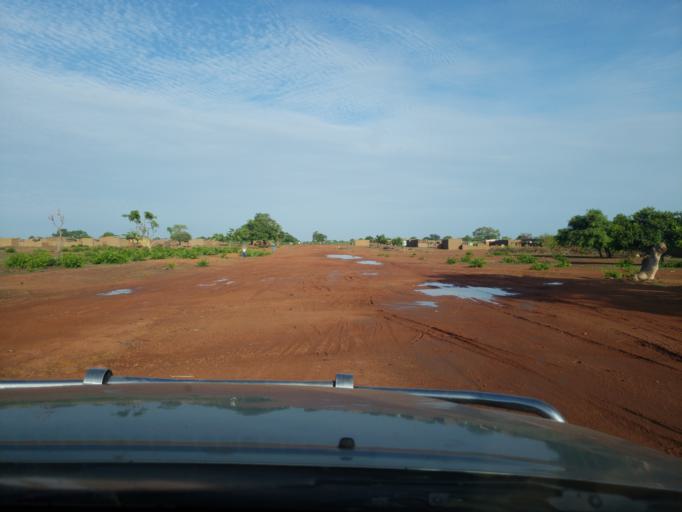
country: ML
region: Sikasso
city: Koutiala
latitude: 12.4288
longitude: -5.6201
